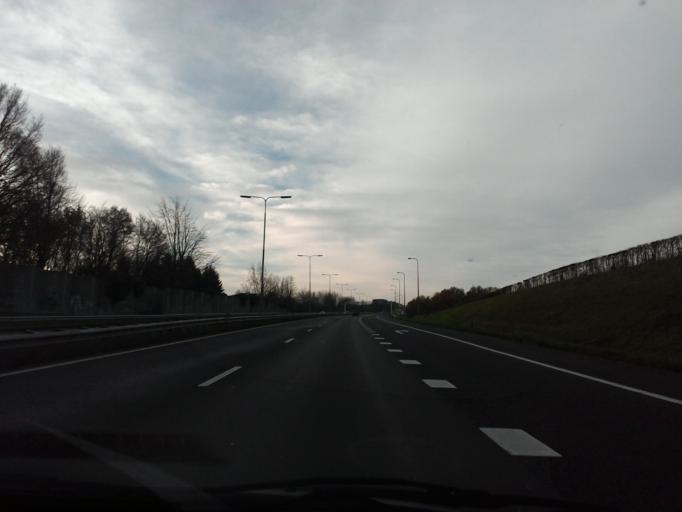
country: NL
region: Limburg
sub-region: Gemeente Beek
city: Beek
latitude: 50.9398
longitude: 5.7866
